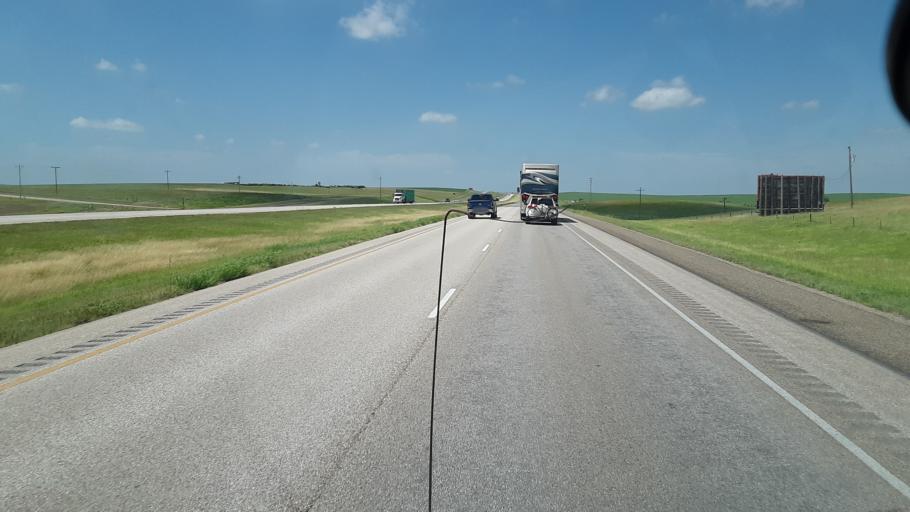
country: US
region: South Dakota
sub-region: Jackson County
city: Kadoka
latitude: 43.8366
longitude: -101.5601
